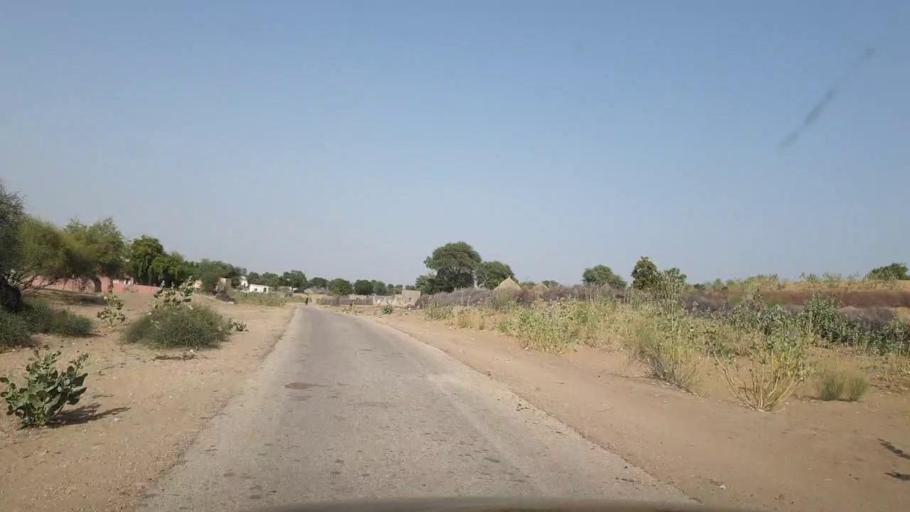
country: PK
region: Sindh
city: Islamkot
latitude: 25.1307
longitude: 70.4556
